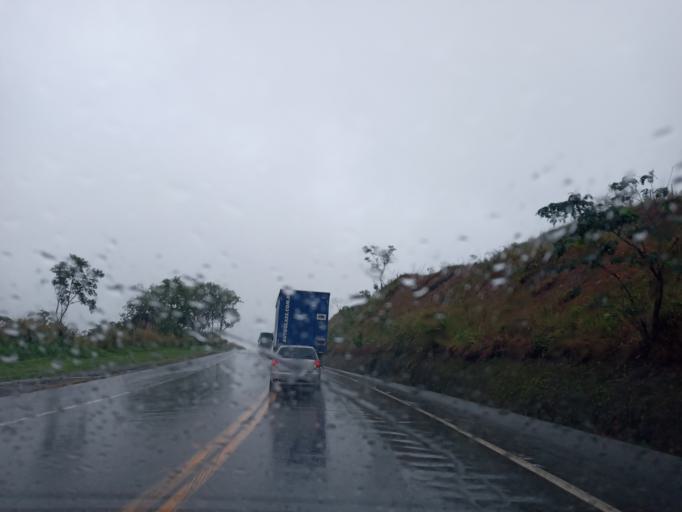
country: BR
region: Minas Gerais
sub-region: Luz
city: Luz
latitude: -19.7152
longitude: -45.8834
